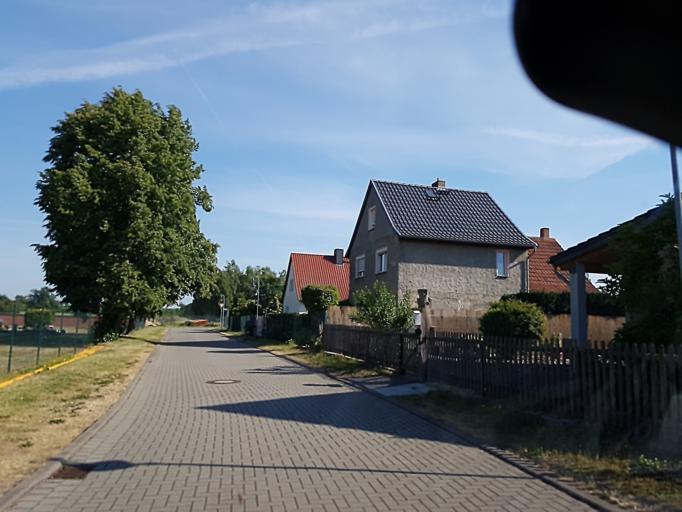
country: DE
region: Saxony-Anhalt
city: Lindau
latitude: 52.0270
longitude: 12.2306
